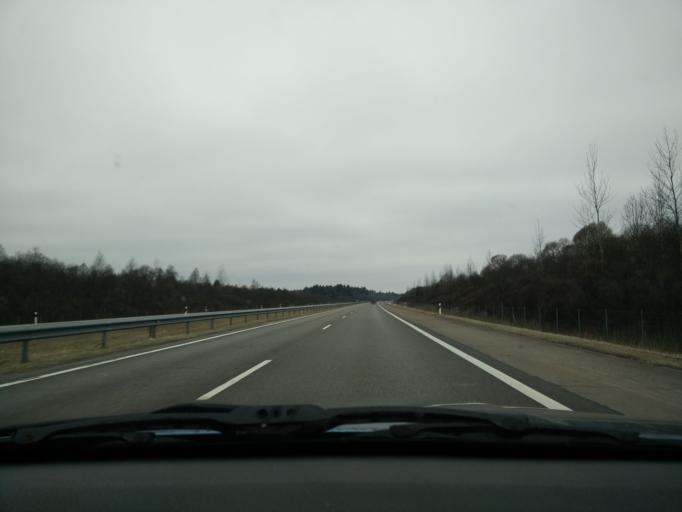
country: LT
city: Rietavas
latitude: 55.6111
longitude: 22.0434
